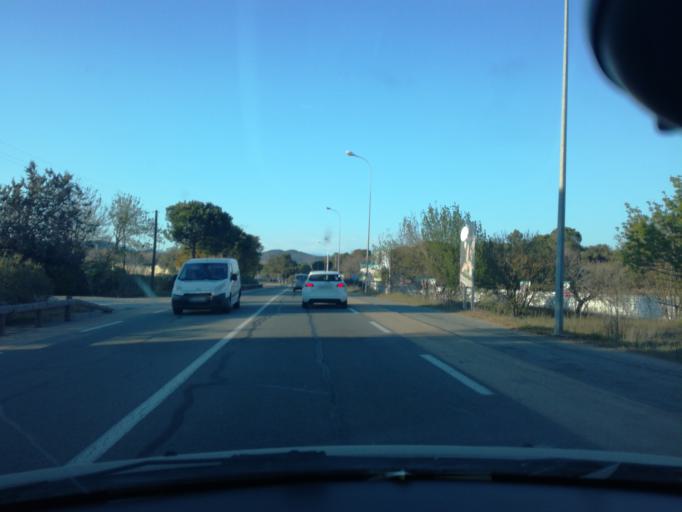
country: FR
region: Provence-Alpes-Cote d'Azur
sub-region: Departement du Var
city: Frejus
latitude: 43.4686
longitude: 6.7445
